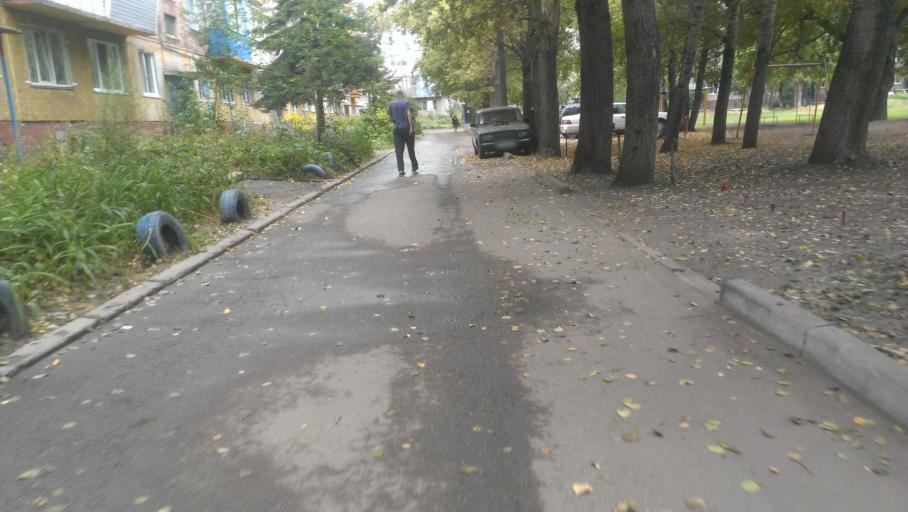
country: RU
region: Altai Krai
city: Novosilikatnyy
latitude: 53.3737
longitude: 83.6710
